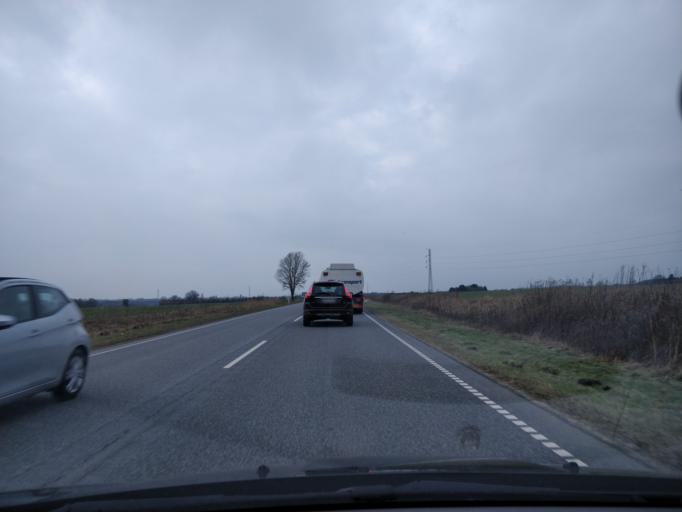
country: DK
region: South Denmark
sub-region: Vejle Kommune
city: Borkop
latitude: 55.6610
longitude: 9.6154
